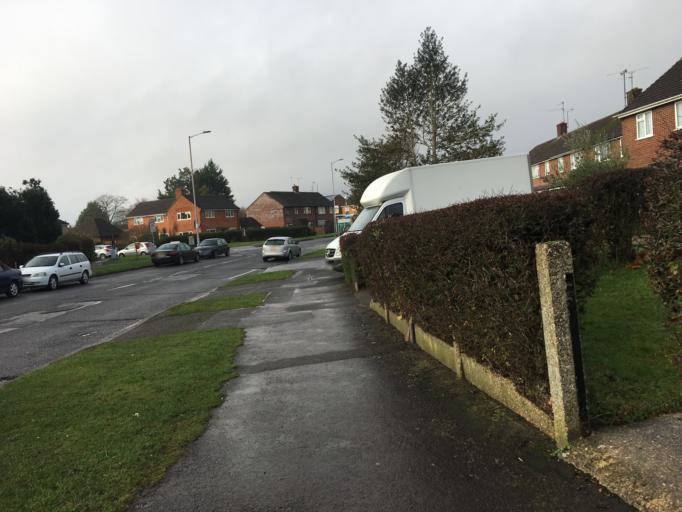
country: GB
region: England
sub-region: West Berkshire
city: Tilehurst
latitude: 51.4416
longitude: -1.0131
